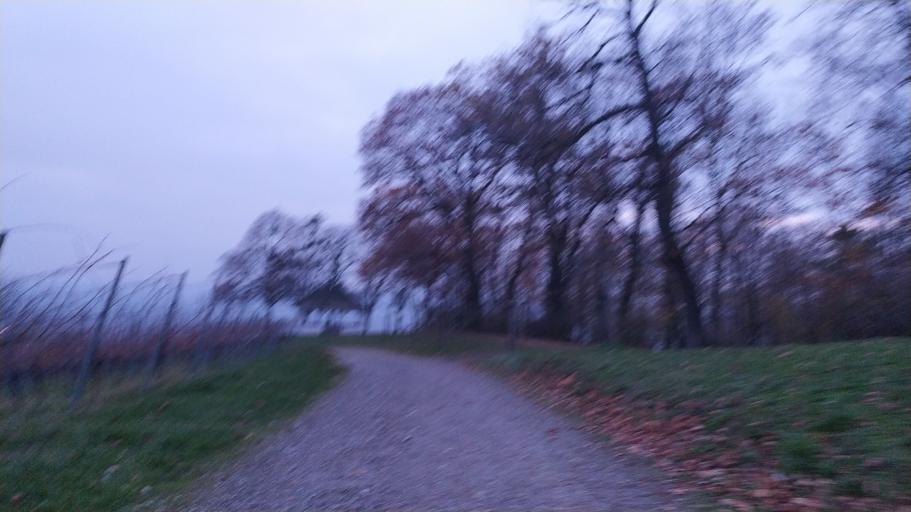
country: DE
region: Hesse
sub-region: Regierungsbezirk Darmstadt
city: Bensheim
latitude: 49.6992
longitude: 8.6311
